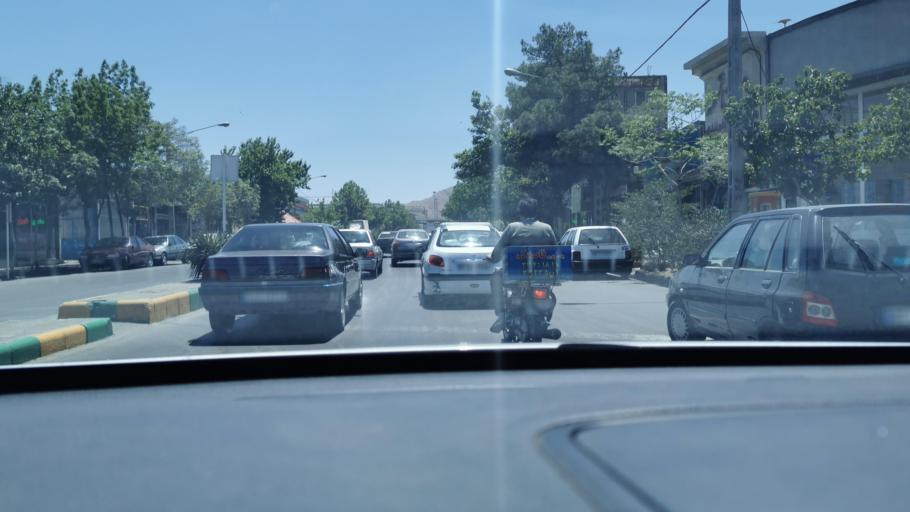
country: IR
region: Razavi Khorasan
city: Mashhad
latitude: 36.2602
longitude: 59.6025
